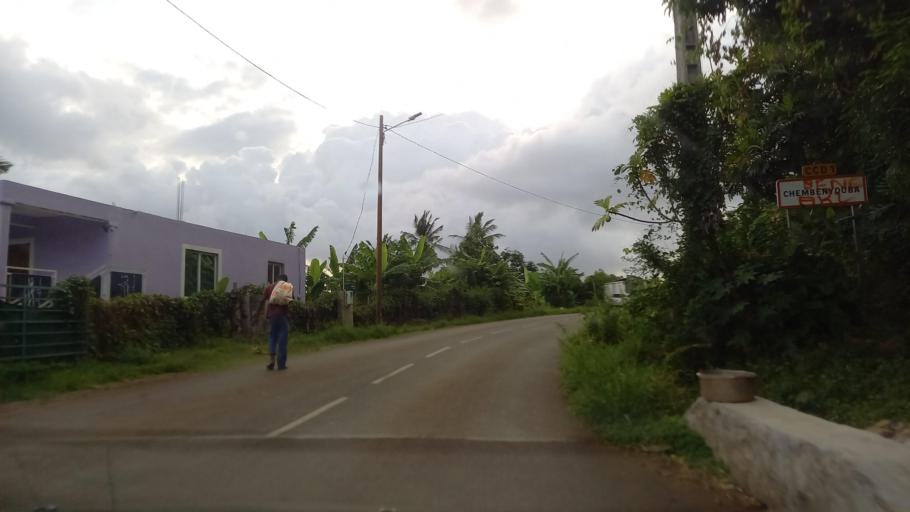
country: YT
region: M'Tsangamouji
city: M'Tsangamouji
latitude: -12.7663
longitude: 45.0789
